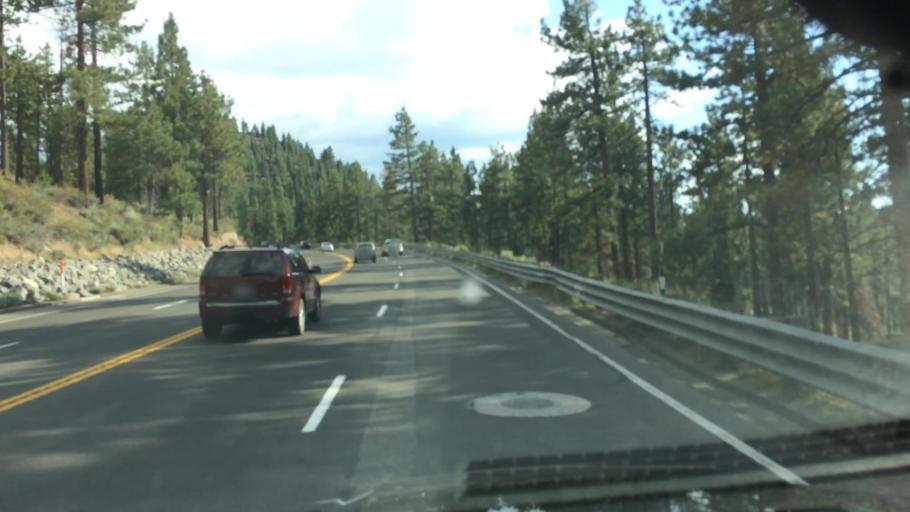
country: US
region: Nevada
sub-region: Douglas County
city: Kingsbury
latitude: 38.9916
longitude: -119.9489
